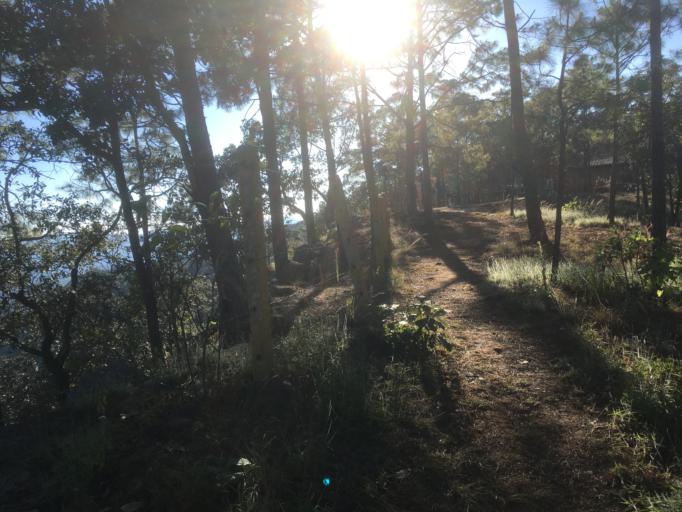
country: MX
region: Michoacan
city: Tzitzio
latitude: 19.6037
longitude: -100.9272
